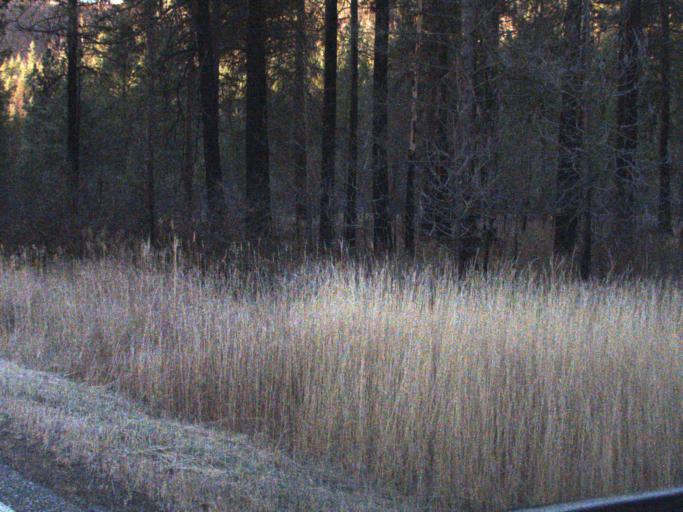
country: US
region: Washington
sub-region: Ferry County
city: Republic
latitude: 48.2984
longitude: -118.7345
